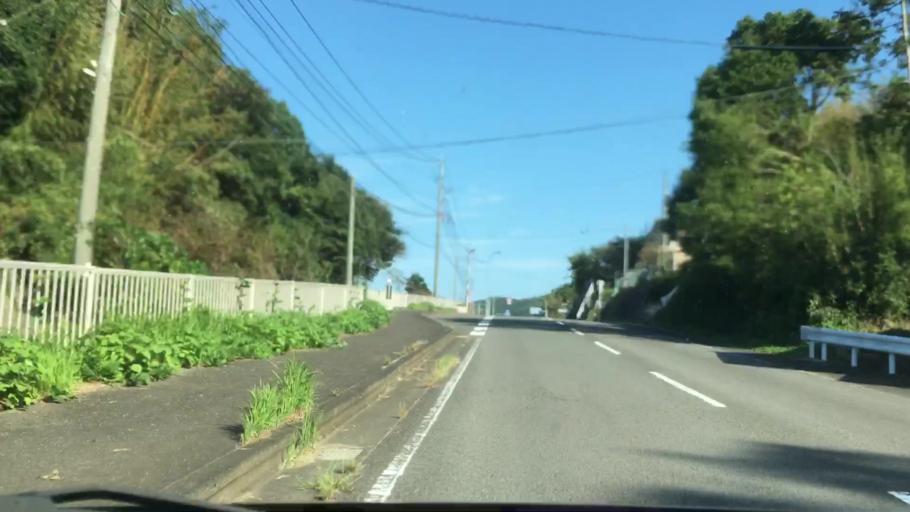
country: JP
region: Nagasaki
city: Sasebo
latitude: 33.0190
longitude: 129.6542
